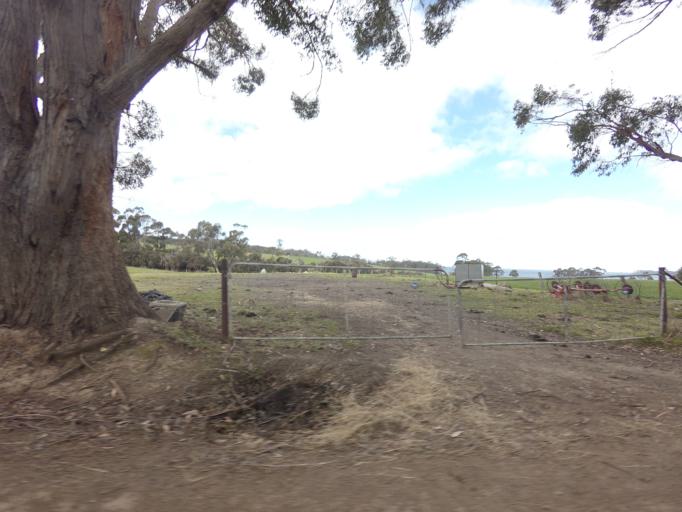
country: AU
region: Tasmania
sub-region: Huon Valley
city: Geeveston
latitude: -43.4294
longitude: 146.9923
